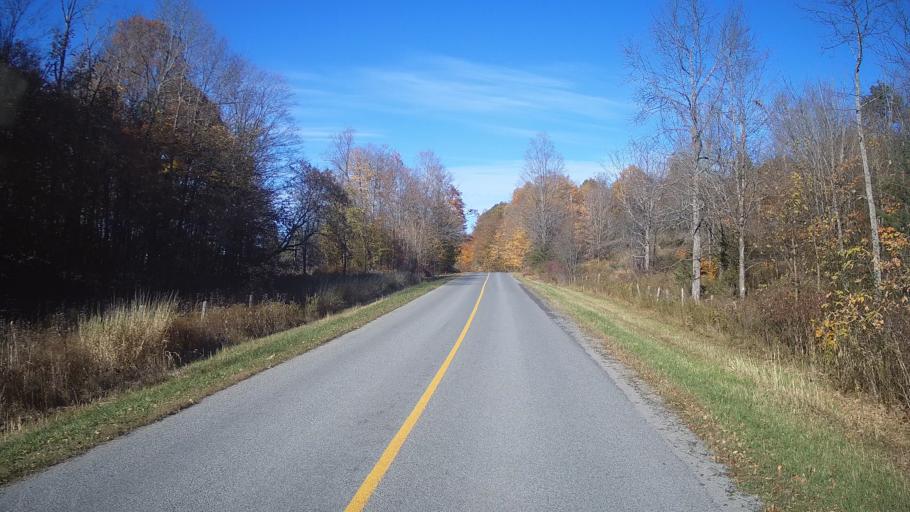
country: CA
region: Ontario
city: Kingston
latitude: 44.4602
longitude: -76.5015
